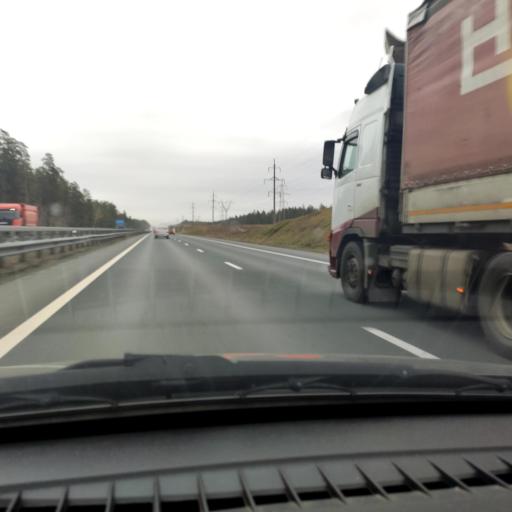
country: RU
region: Samara
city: Povolzhskiy
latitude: 53.5164
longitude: 49.7478
